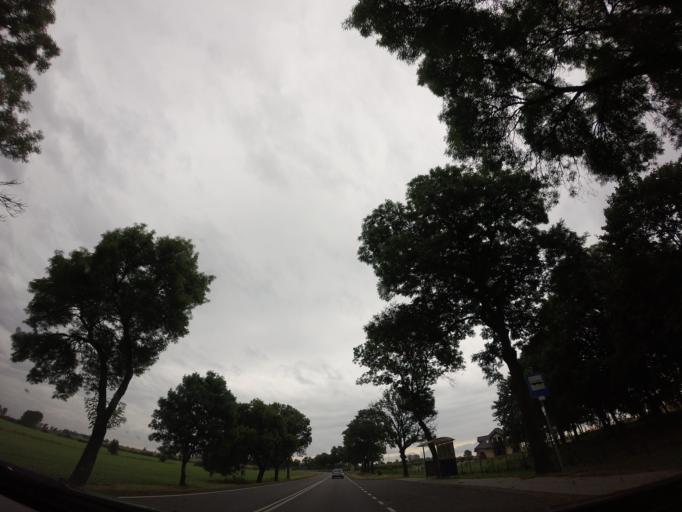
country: PL
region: Masovian Voivodeship
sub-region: Powiat plocki
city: Drobin
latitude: 52.7537
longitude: 20.0413
